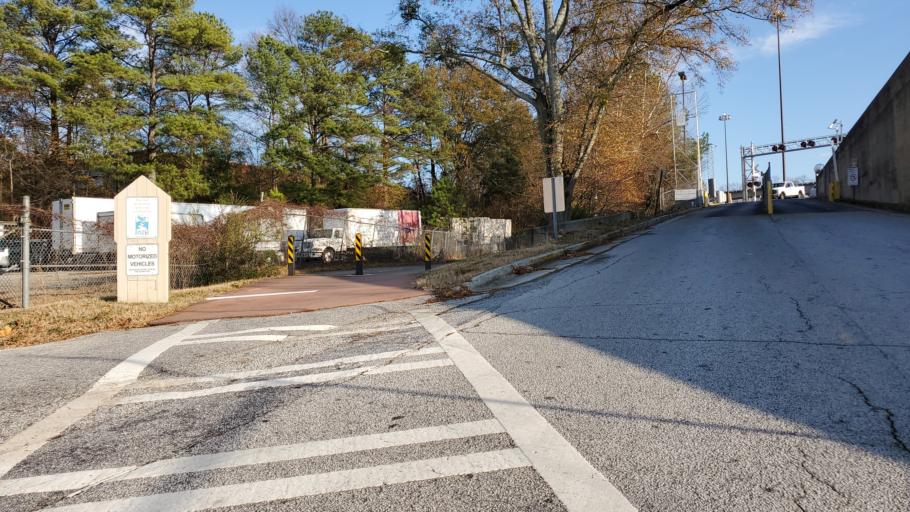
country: US
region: Georgia
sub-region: DeKalb County
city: Avondale Estates
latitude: 33.7802
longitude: -84.2727
